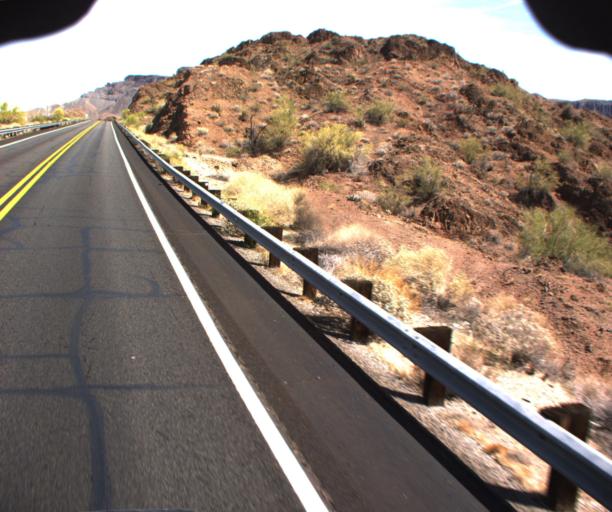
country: US
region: Arizona
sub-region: La Paz County
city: Cienega Springs
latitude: 34.2935
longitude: -114.1258
